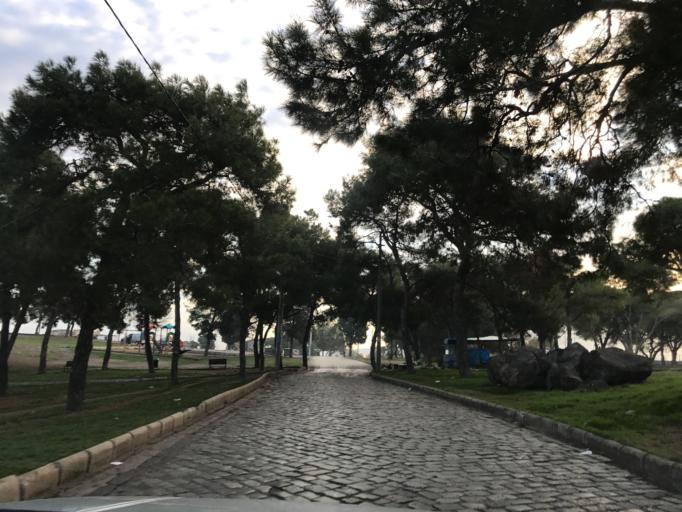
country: TR
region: Izmir
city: Izmir
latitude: 38.4139
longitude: 27.1464
